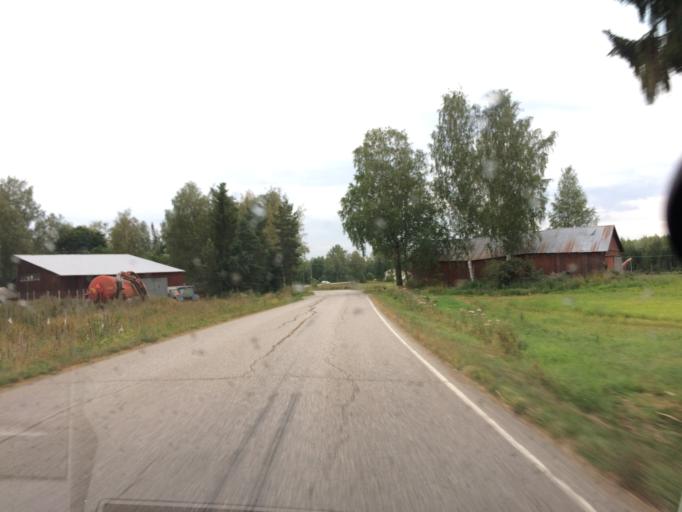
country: FI
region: Haeme
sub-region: Haemeenlinna
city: Tuulos
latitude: 61.1839
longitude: 24.7614
